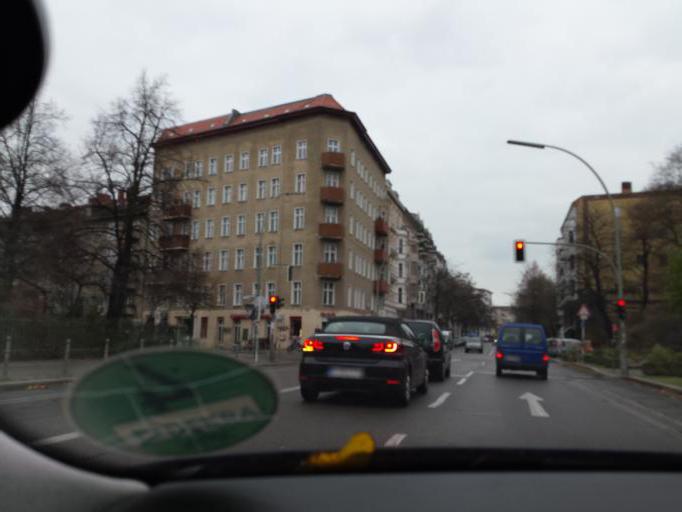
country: DE
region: Berlin
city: Bezirk Kreuzberg
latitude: 52.4898
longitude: 13.3817
